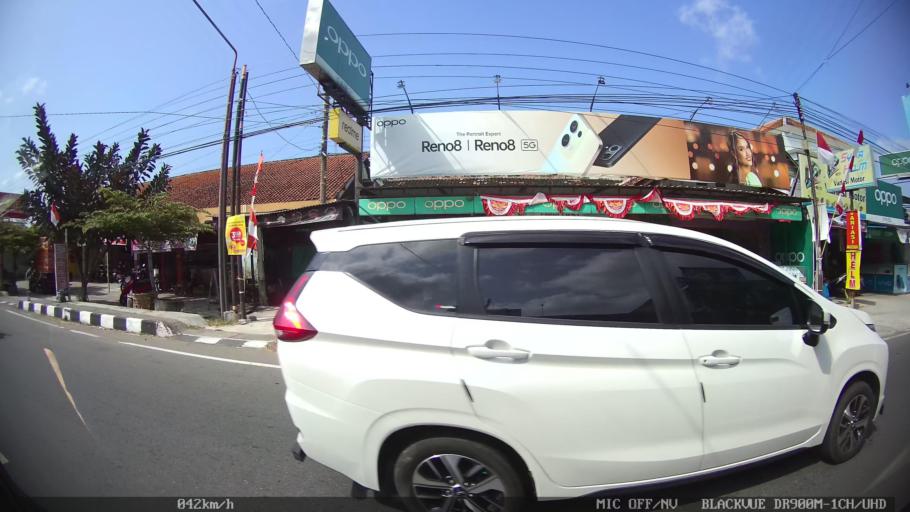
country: ID
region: Daerah Istimewa Yogyakarta
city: Srandakan
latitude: -7.8952
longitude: 110.1509
